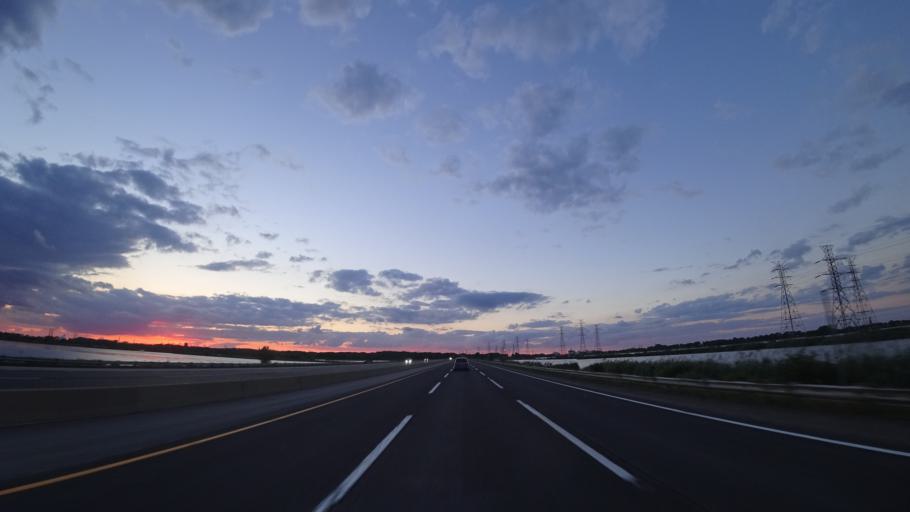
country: US
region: Indiana
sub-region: Lake County
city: Whiting
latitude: 41.6649
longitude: -87.5187
